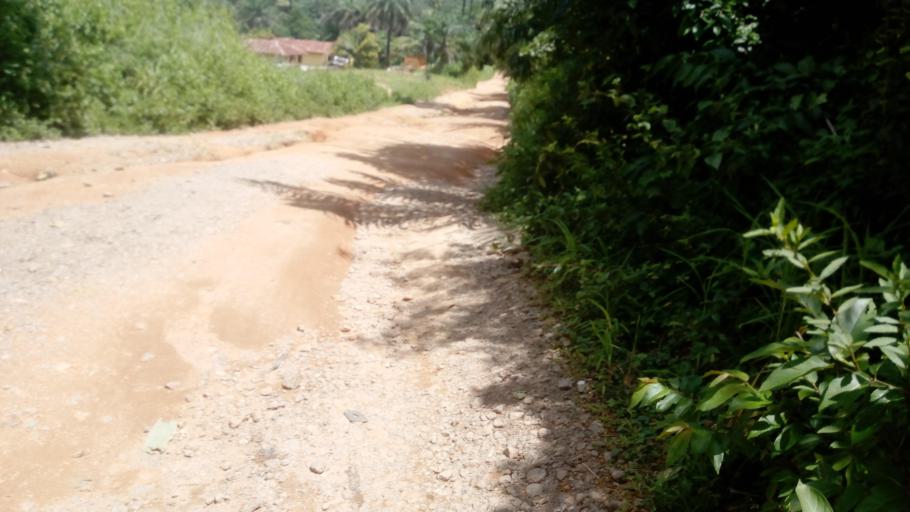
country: SL
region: Northern Province
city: Binkolo
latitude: 8.9537
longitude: -11.9752
